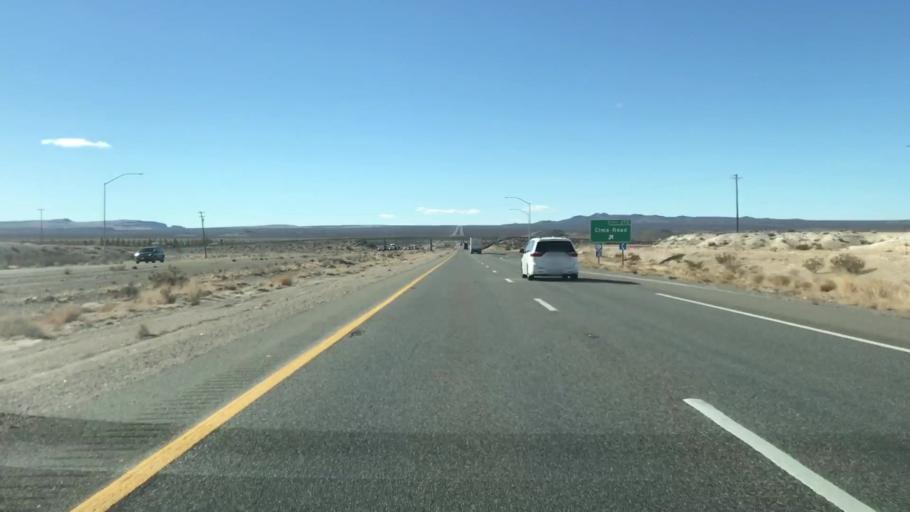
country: US
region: Nevada
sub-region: Clark County
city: Sandy Valley
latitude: 35.4456
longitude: -115.6691
